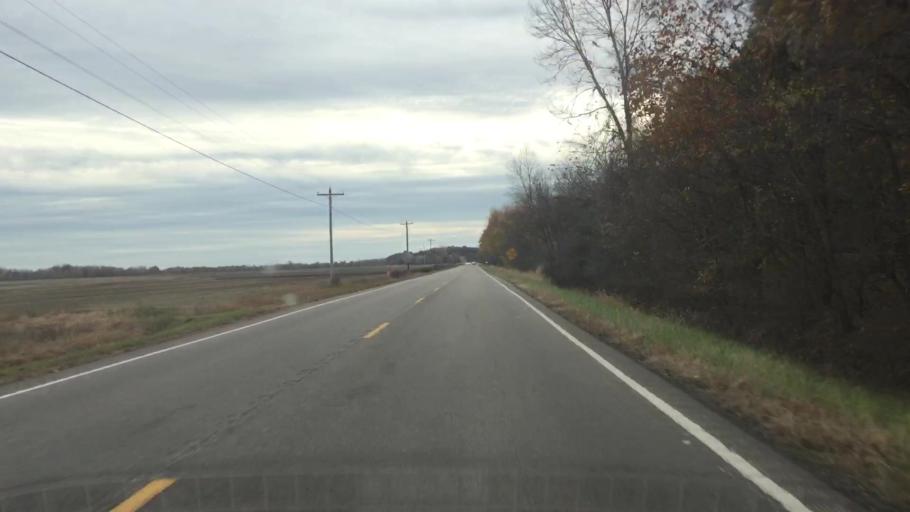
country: US
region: Missouri
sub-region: Callaway County
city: Fulton
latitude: 38.6933
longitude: -91.8371
